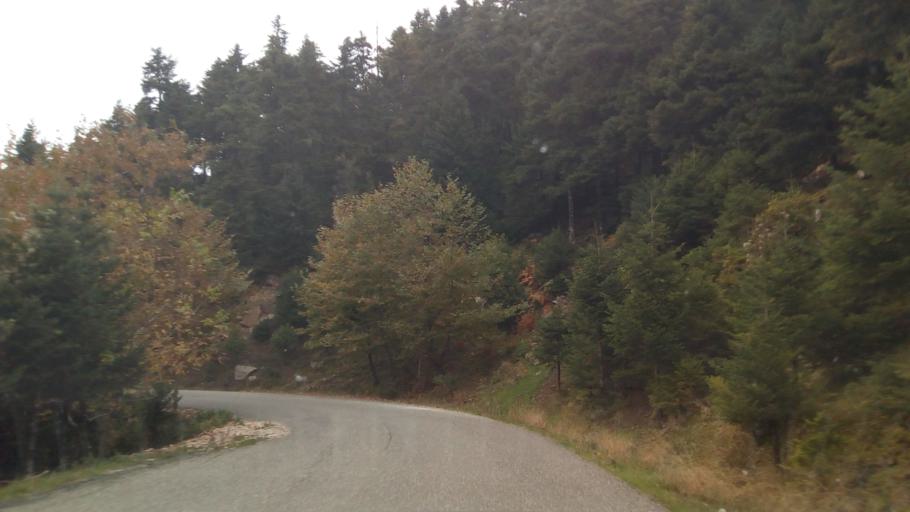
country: GR
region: West Greece
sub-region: Nomos Aitolias kai Akarnanias
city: Thermo
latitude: 38.6313
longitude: 21.8316
